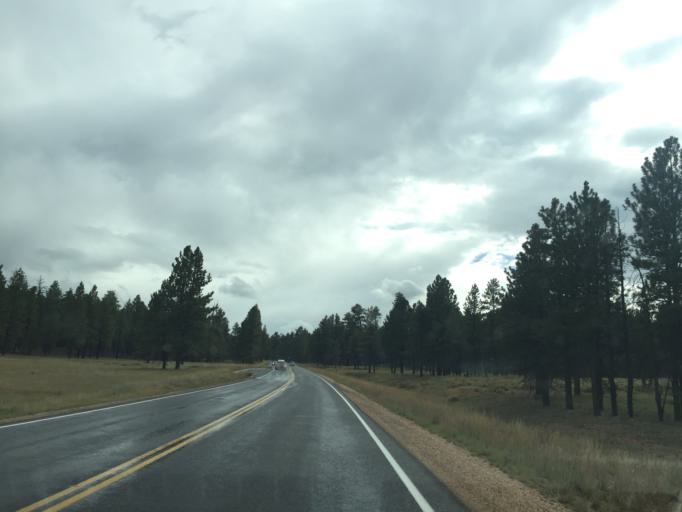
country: US
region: Utah
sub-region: Garfield County
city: Panguitch
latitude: 37.6368
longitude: -112.1719
